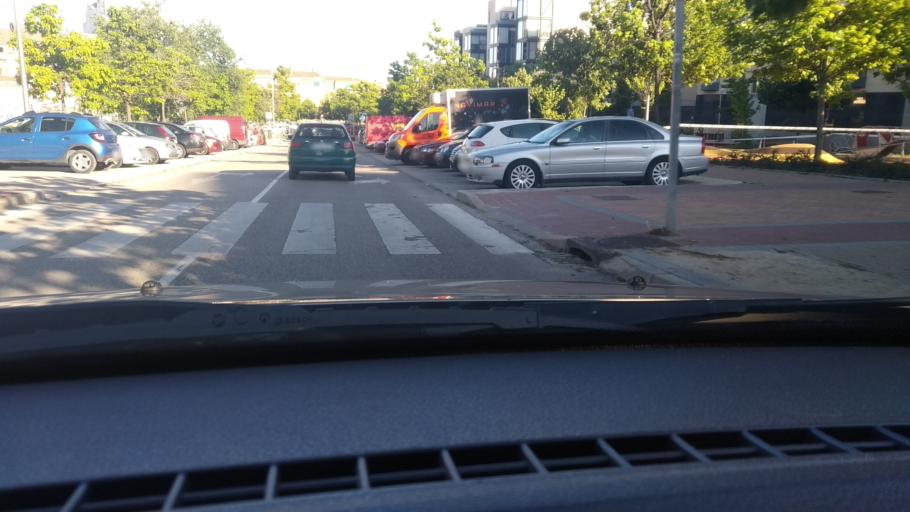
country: ES
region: Madrid
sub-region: Provincia de Madrid
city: Villa de Vallecas
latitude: 40.3770
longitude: -3.6262
